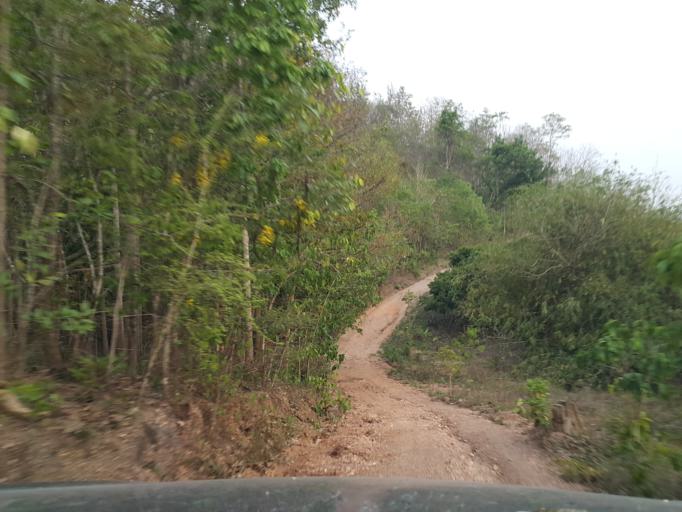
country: TH
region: Lamphun
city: Thung Hua Chang
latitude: 17.8993
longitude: 99.0825
